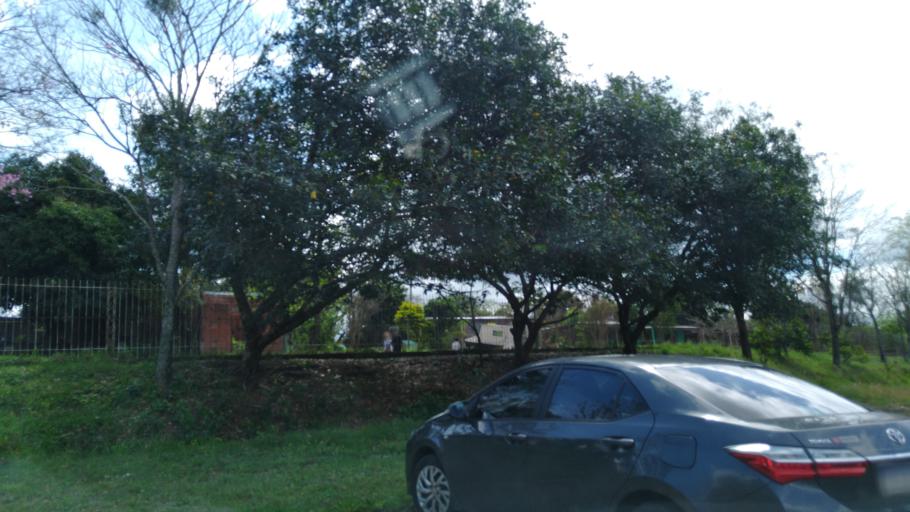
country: AR
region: Misiones
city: Garupa
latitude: -27.4603
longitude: -55.8440
